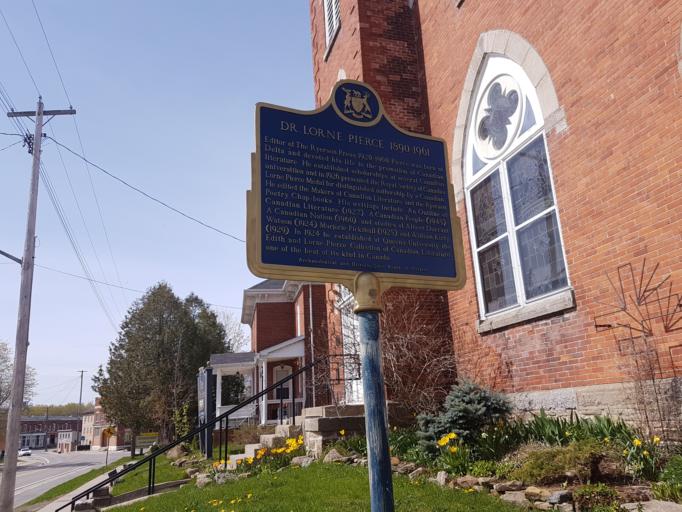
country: CA
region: Ontario
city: Gananoque
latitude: 44.6114
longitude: -76.1219
